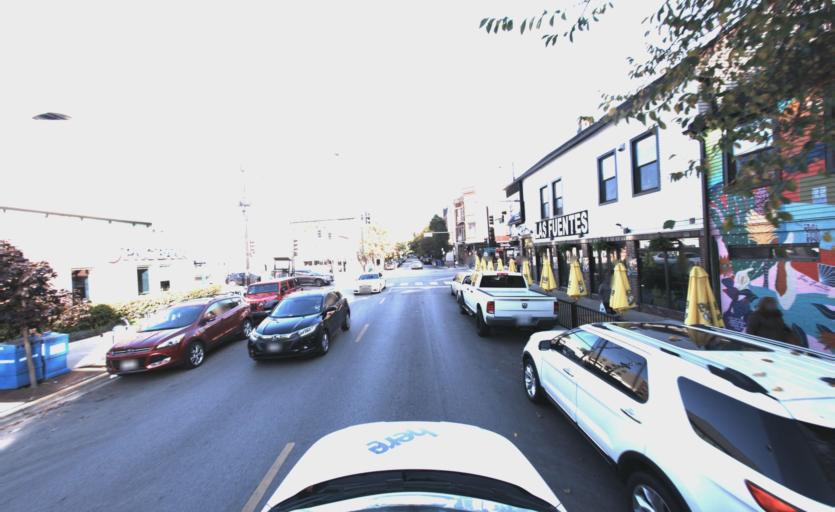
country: US
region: Illinois
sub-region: Cook County
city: Chicago
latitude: 41.9291
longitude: -87.6493
